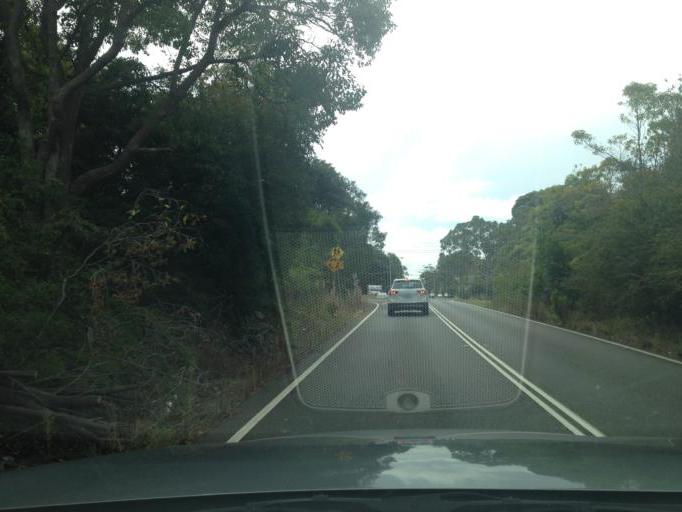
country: AU
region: New South Wales
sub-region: Ku-ring-gai
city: Lindfield
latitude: -33.7787
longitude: 151.1513
